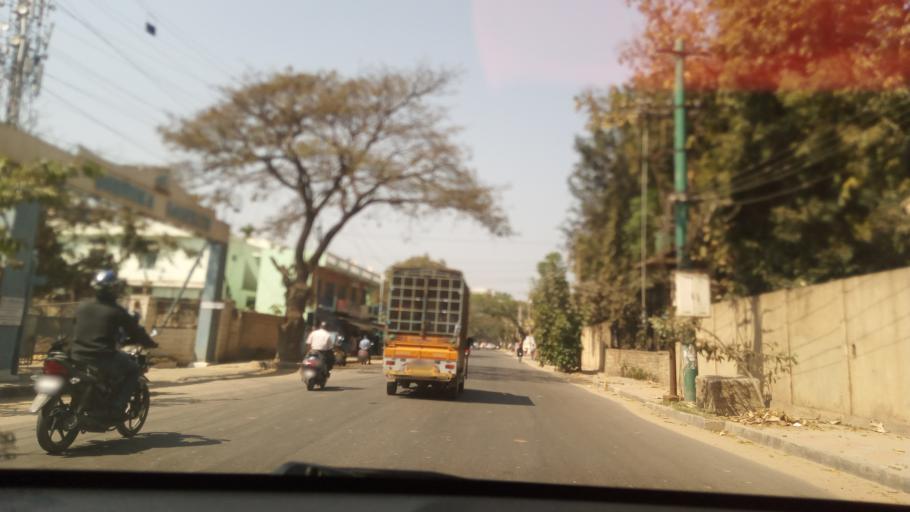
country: IN
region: Karnataka
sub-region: Bangalore Urban
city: Bangalore
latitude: 12.9895
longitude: 77.7068
